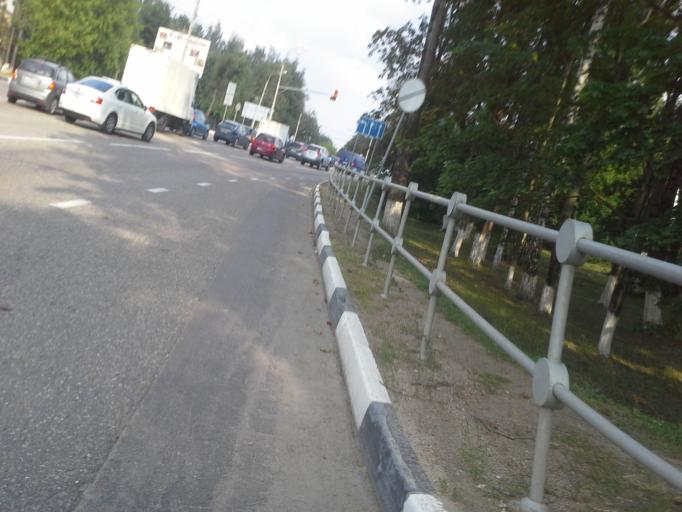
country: RU
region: Moskovskaya
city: Istra
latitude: 55.9206
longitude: 36.8566
